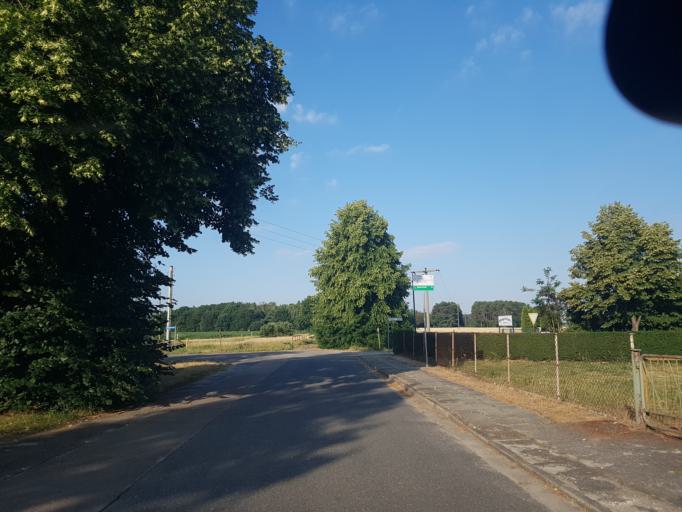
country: DE
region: Saxony-Anhalt
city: Holzdorf
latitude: 51.7954
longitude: 13.1751
